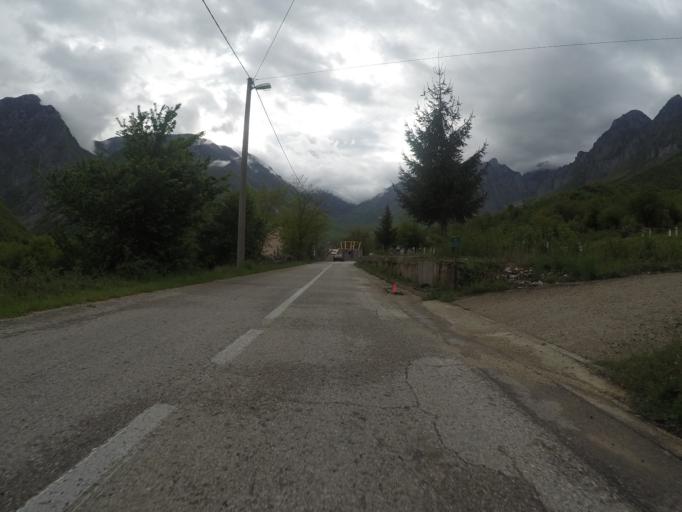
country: BA
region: Federation of Bosnia and Herzegovina
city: Siroki Brijeg
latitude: 43.5406
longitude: 17.5853
